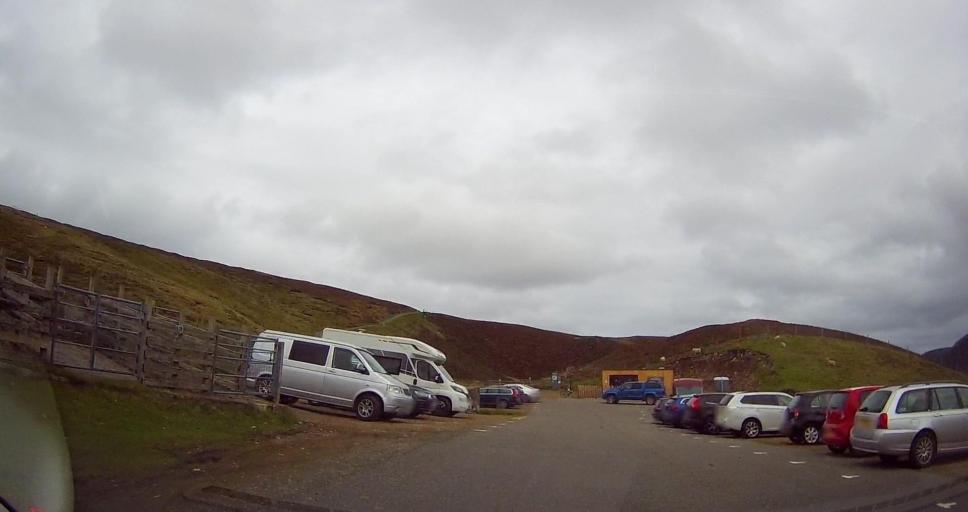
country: GB
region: Scotland
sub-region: Shetland Islands
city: Shetland
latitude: 60.8121
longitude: -0.8765
